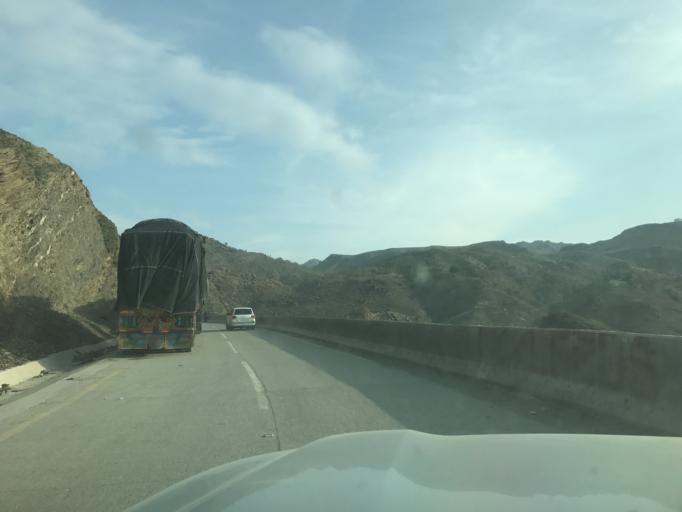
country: PK
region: Federally Administered Tribal Areas
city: Landi Kotal
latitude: 34.1118
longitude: 71.1127
